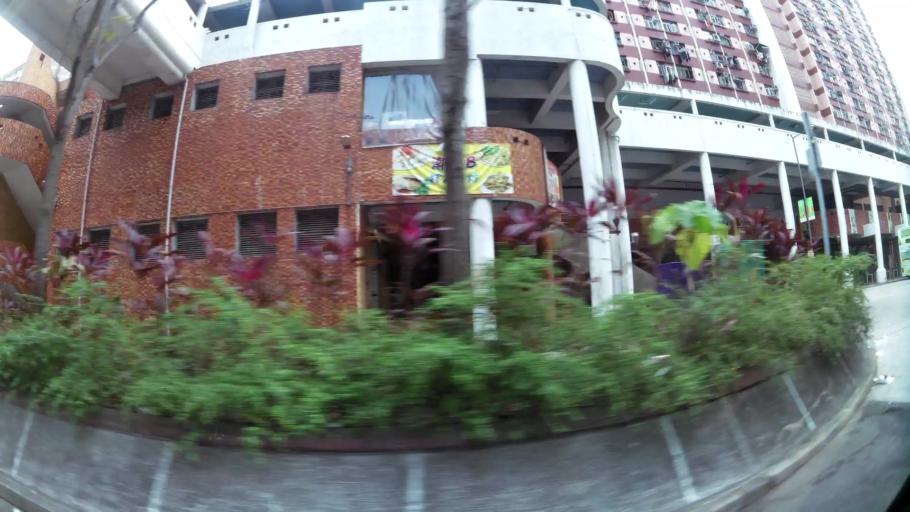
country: HK
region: Kowloon City
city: Kowloon
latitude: 22.3161
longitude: 114.2294
